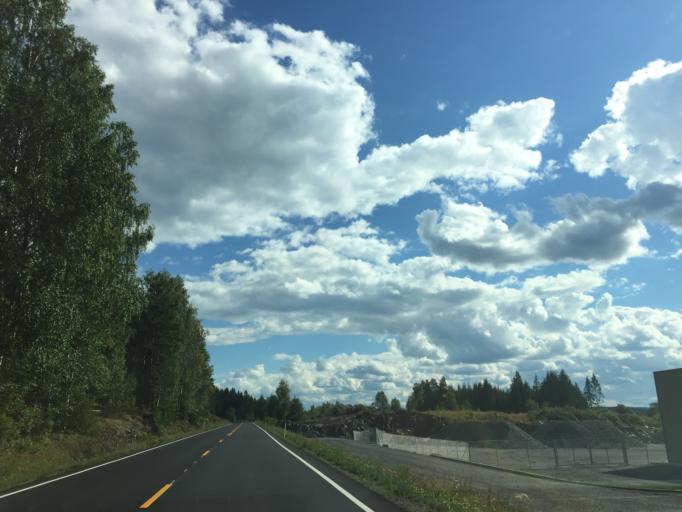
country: NO
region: Hedmark
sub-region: Sor-Odal
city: Skarnes
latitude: 60.2369
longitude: 11.6772
